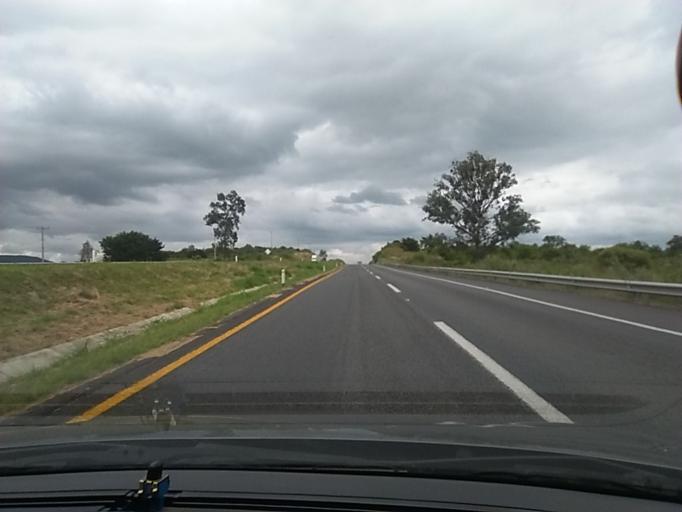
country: MX
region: Jalisco
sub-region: Zapotlanejo
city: La Mezquitera
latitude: 20.5567
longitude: -103.0653
